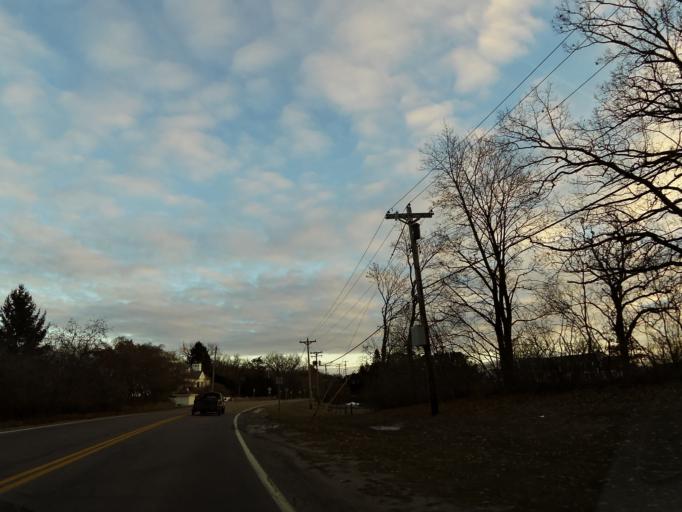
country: US
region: Minnesota
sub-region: Washington County
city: Dellwood
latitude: 45.0918
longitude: -92.9749
